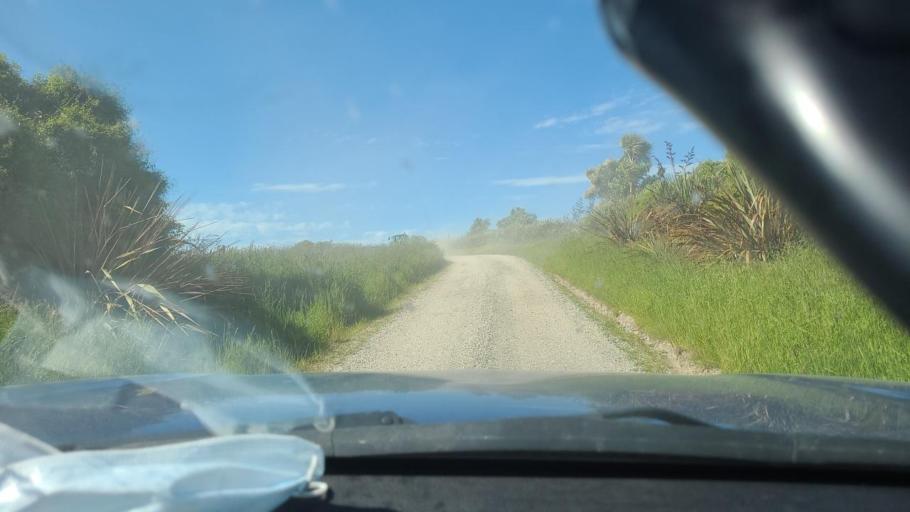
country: NZ
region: Southland
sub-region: Gore District
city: Gore
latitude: -46.5015
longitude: 168.8249
